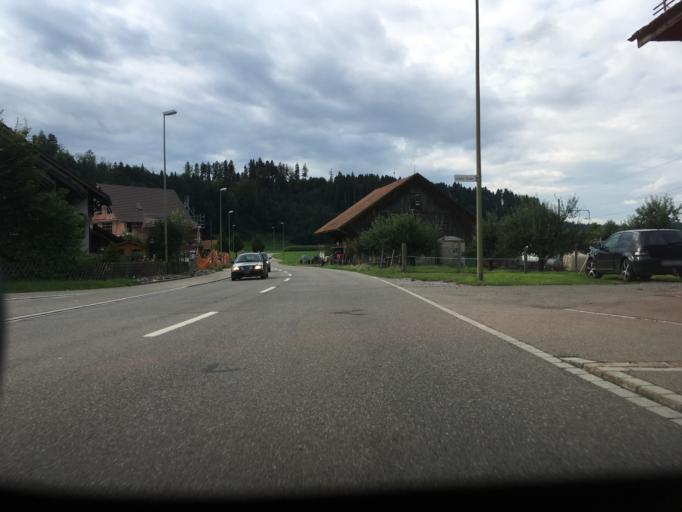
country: CH
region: Zurich
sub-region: Bezirk Pfaeffikon
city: Bauma
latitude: 47.3810
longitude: 8.8592
